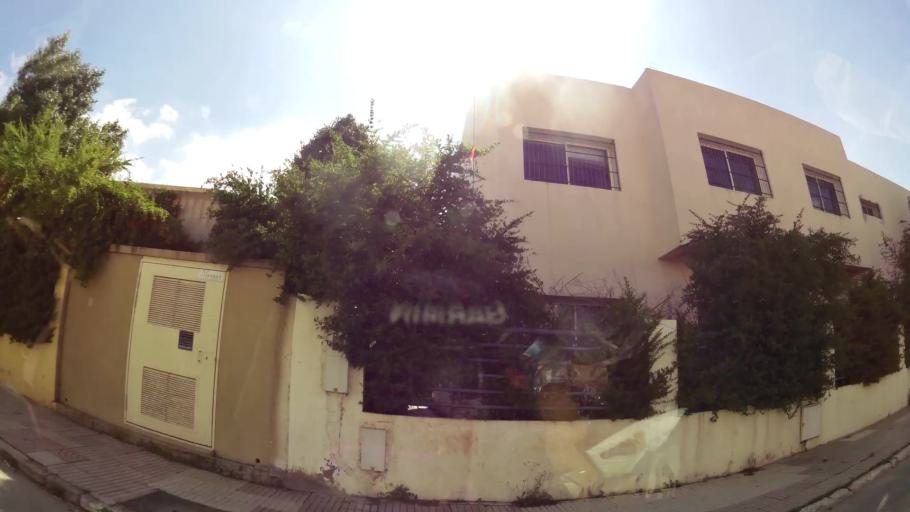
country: MA
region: Fes-Boulemane
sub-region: Fes
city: Fes
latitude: 34.0325
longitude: -5.0274
